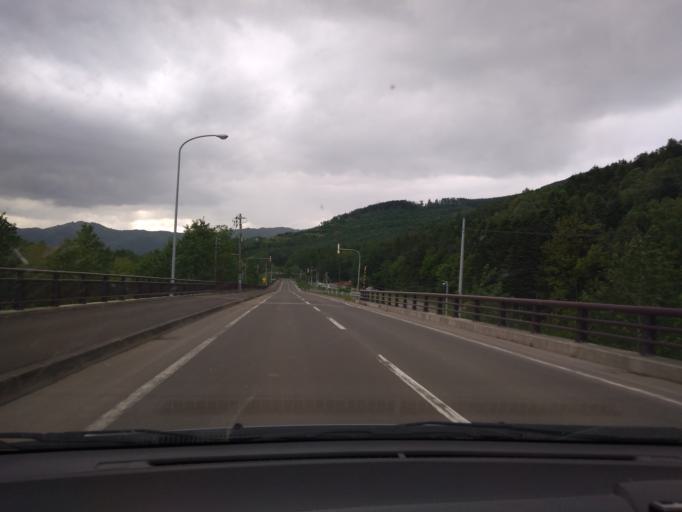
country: JP
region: Hokkaido
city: Shimo-furano
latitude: 43.1724
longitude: 142.5652
